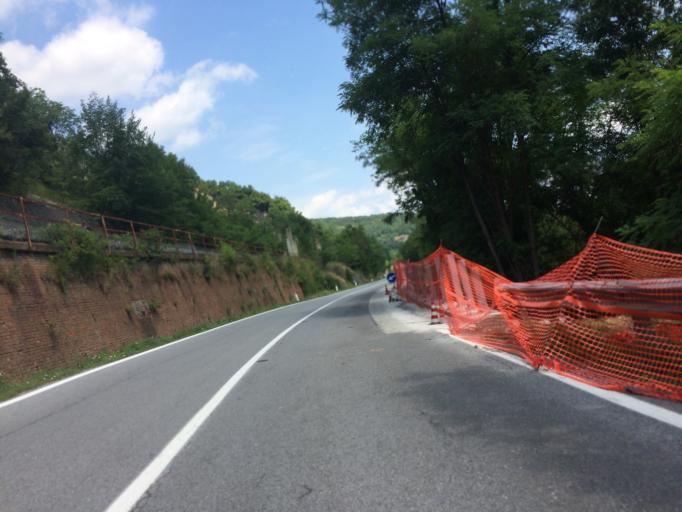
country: IT
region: Piedmont
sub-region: Provincia di Cuneo
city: Bagnasco
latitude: 44.2850
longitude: 8.0326
